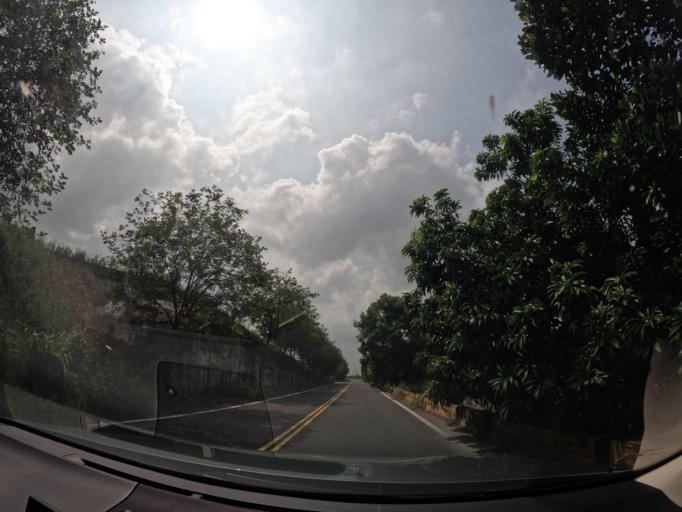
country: TW
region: Taiwan
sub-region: Chiayi
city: Taibao
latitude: 23.6118
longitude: 120.3657
